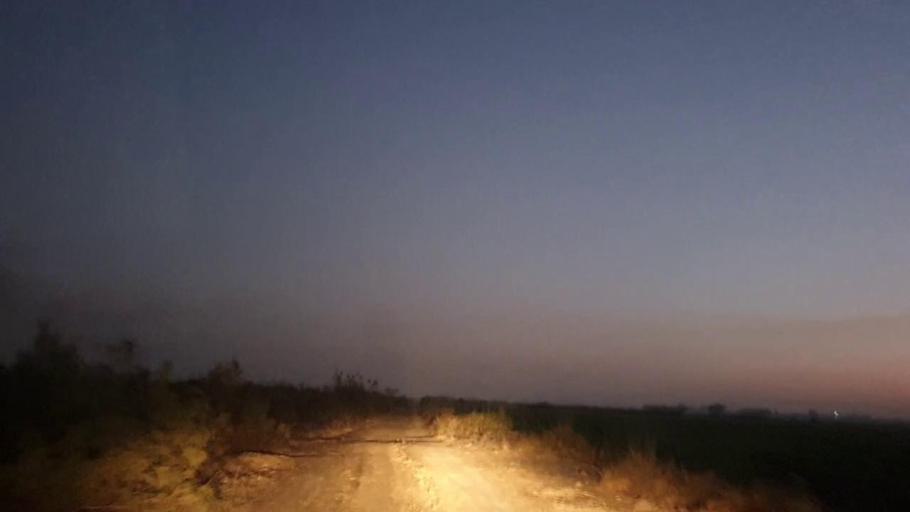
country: PK
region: Sindh
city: Nawabshah
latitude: 26.3237
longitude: 68.3781
